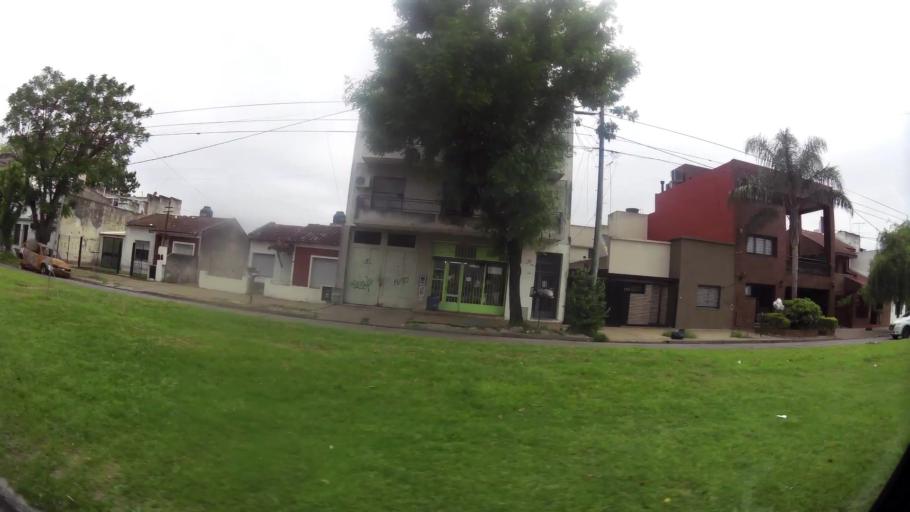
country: AR
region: Buenos Aires
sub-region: Partido de La Plata
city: La Plata
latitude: -34.9266
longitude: -57.9851
